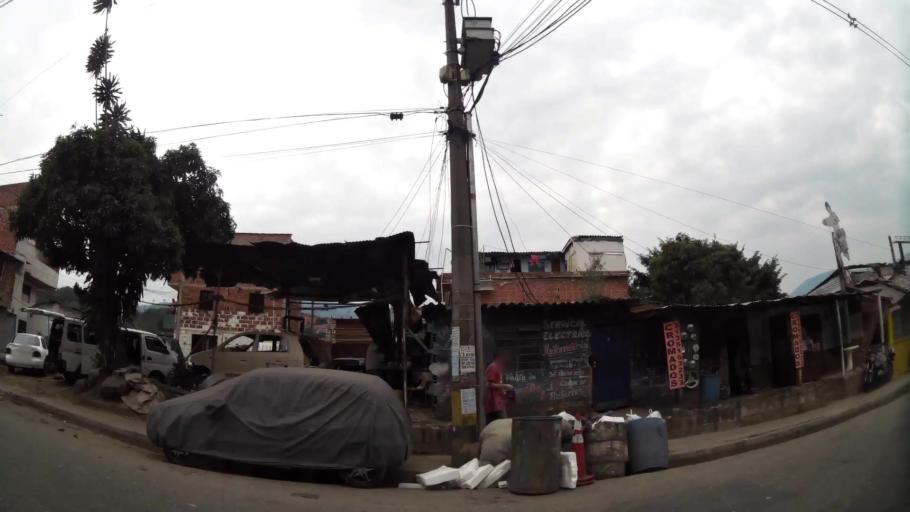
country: CO
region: Antioquia
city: Medellin
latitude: 6.2943
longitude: -75.5609
